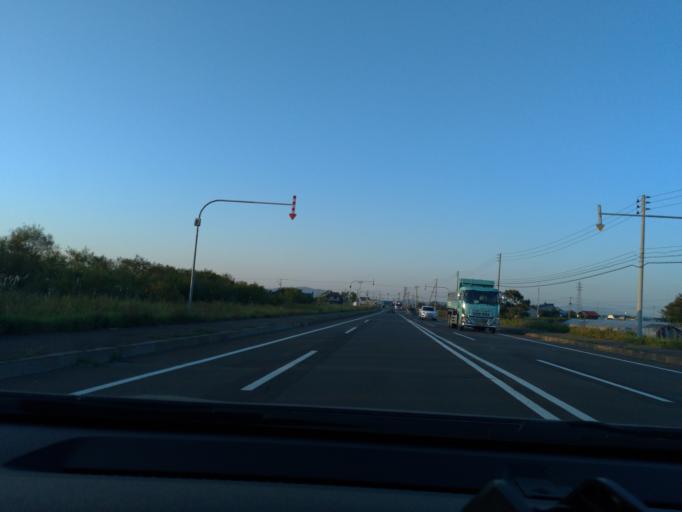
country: JP
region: Hokkaido
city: Tobetsu
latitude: 43.1872
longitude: 141.5241
